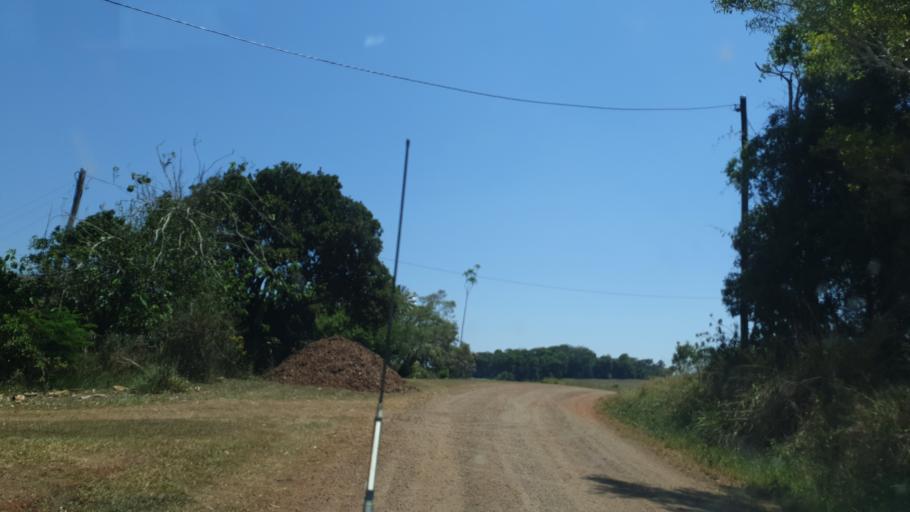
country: AU
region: Queensland
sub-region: Tablelands
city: Atherton
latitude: -17.3488
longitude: 145.6219
